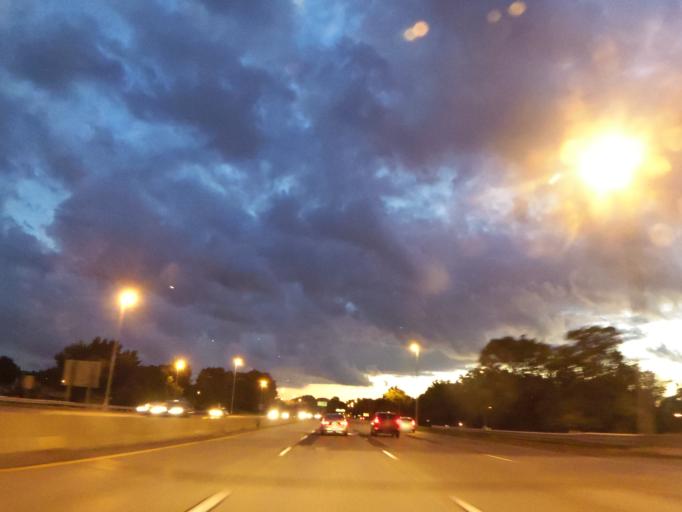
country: US
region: Missouri
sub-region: Saint Louis County
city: Lemay
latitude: 38.5532
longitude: -90.2714
